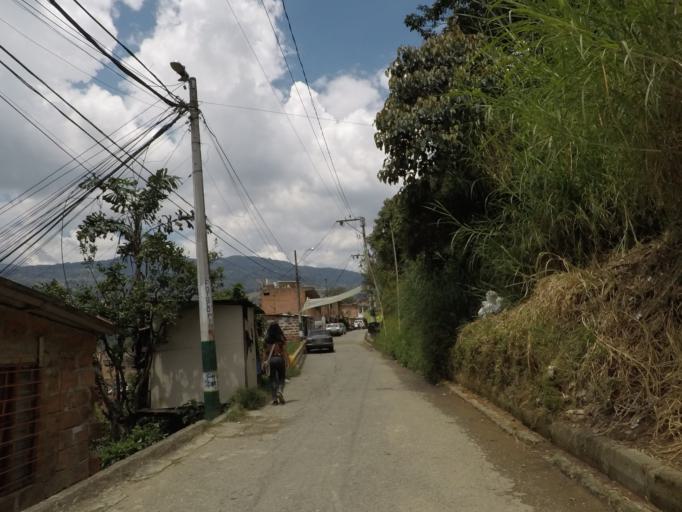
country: CO
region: Antioquia
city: Medellin
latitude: 6.2708
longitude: -75.6266
